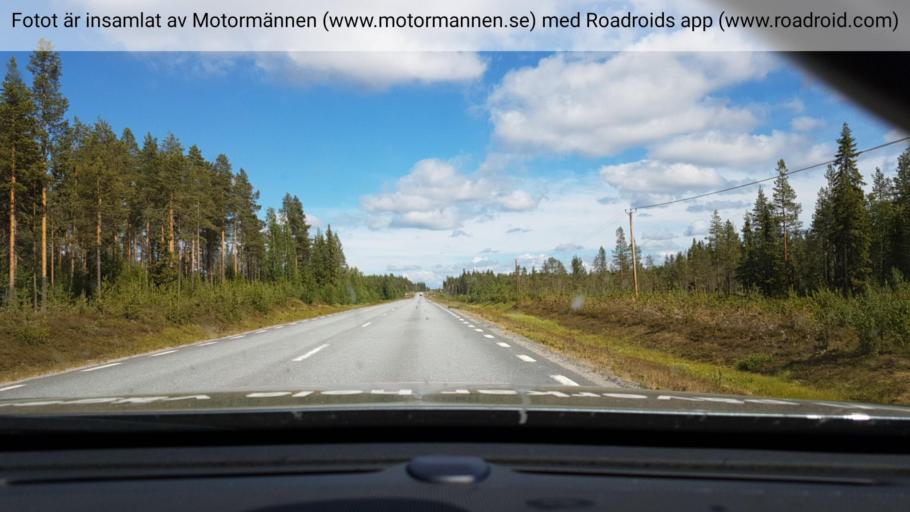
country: SE
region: Vaesterbotten
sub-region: Sorsele Kommun
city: Sorsele
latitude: 65.5575
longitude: 17.7680
